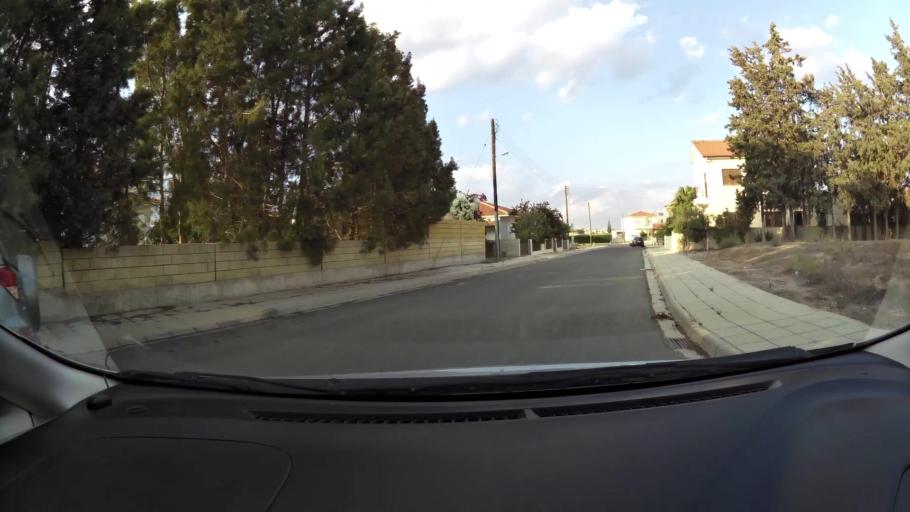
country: CY
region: Larnaka
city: Meneou
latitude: 34.8630
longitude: 33.5826
